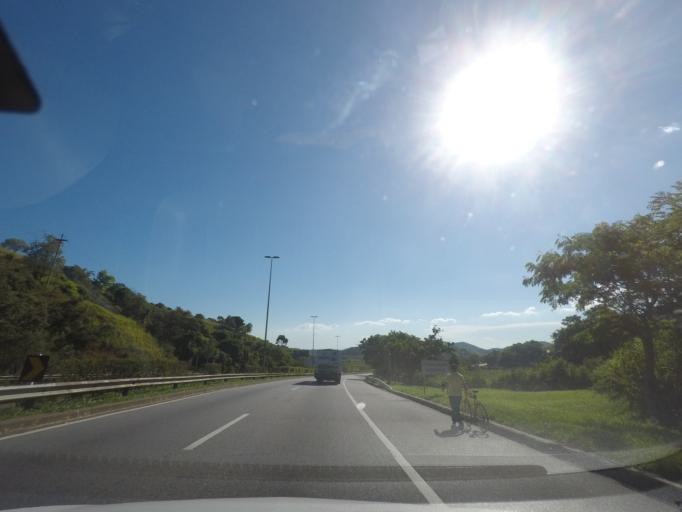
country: BR
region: Rio de Janeiro
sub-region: Sao Goncalo
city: Sao Goncalo
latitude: -22.6640
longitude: -43.0955
